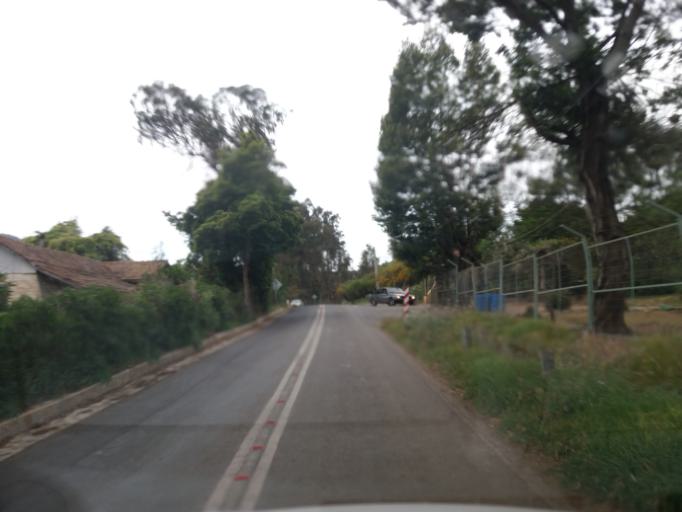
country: CL
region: Valparaiso
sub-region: Provincia de Quillota
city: Quillota
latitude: -32.8912
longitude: -71.3086
